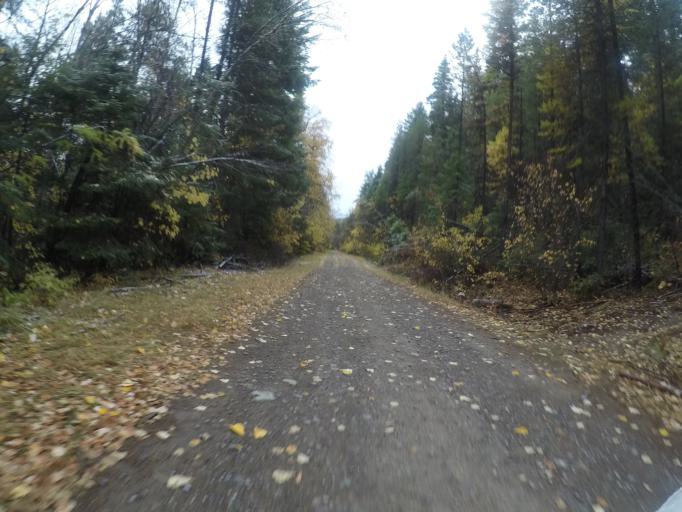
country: US
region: Montana
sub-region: Flathead County
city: Bigfork
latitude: 47.8845
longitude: -113.8757
